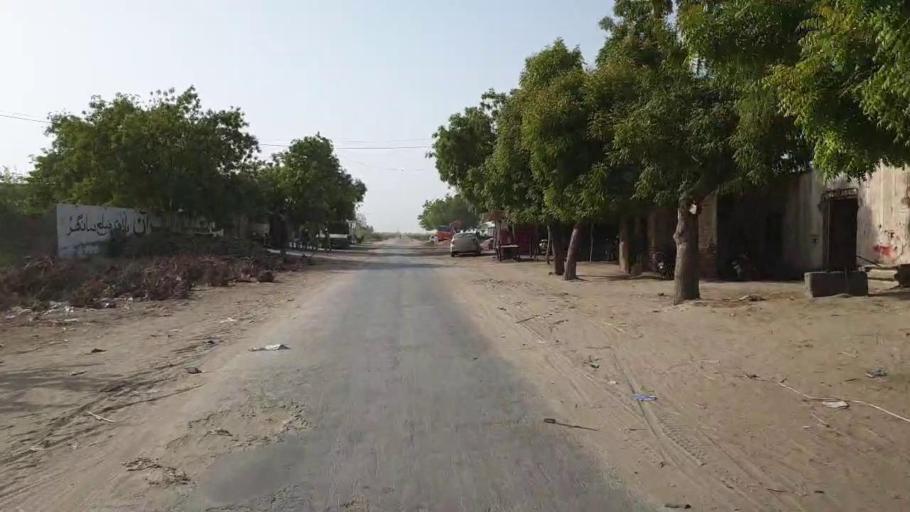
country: PK
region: Sindh
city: Khadro
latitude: 26.3375
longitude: 68.9274
